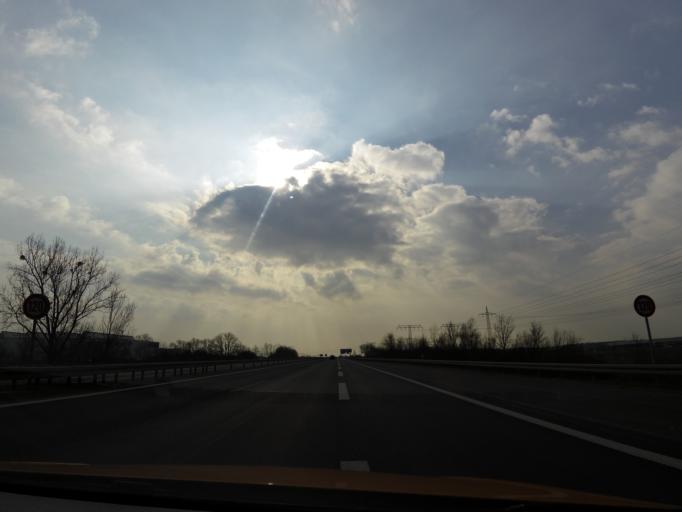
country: DE
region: Brandenburg
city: Ludwigsfelde
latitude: 52.3161
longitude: 13.2874
